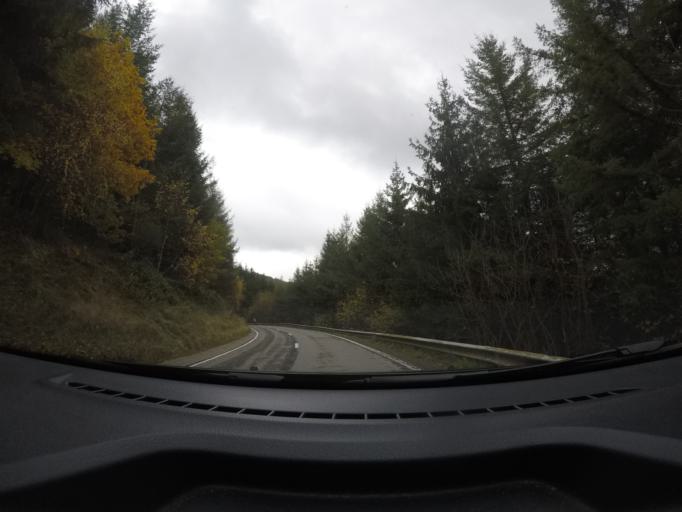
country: BE
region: Wallonia
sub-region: Province du Luxembourg
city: Houffalize
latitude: 50.1393
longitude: 5.7162
